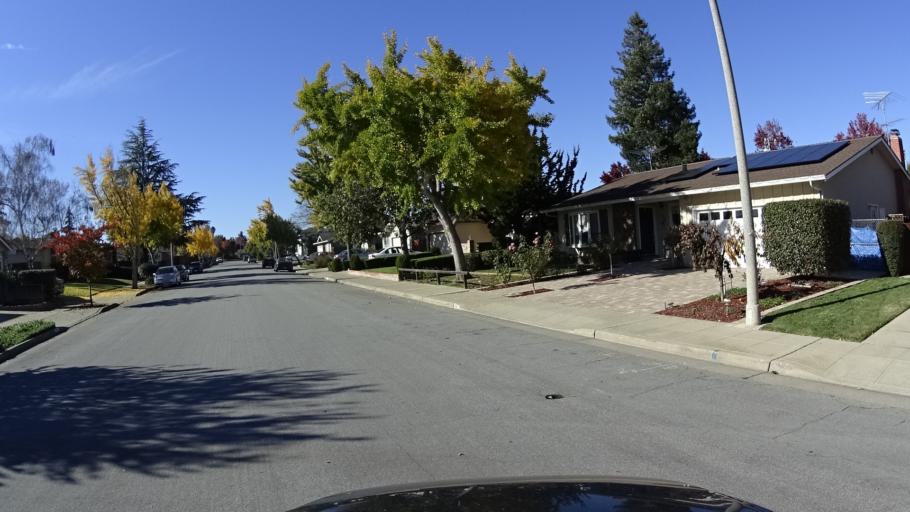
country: US
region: California
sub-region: Santa Clara County
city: Sunnyvale
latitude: 37.3611
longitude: -122.0104
